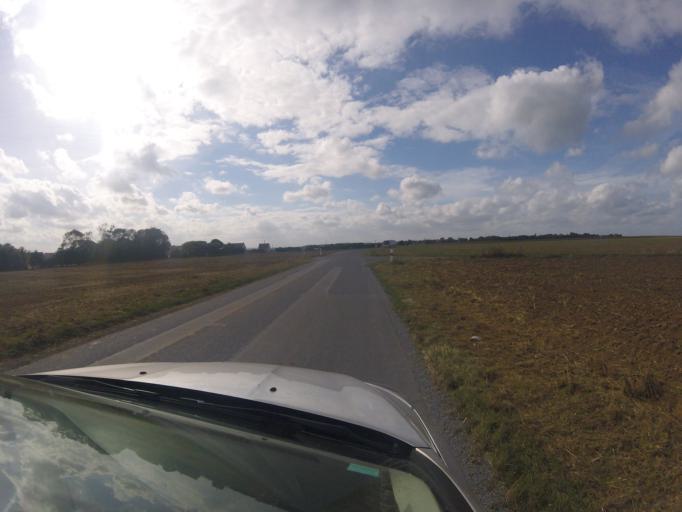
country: FR
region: Lower Normandy
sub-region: Departement du Calvados
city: Saint-Vigor-le-Grand
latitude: 49.3325
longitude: -0.6775
